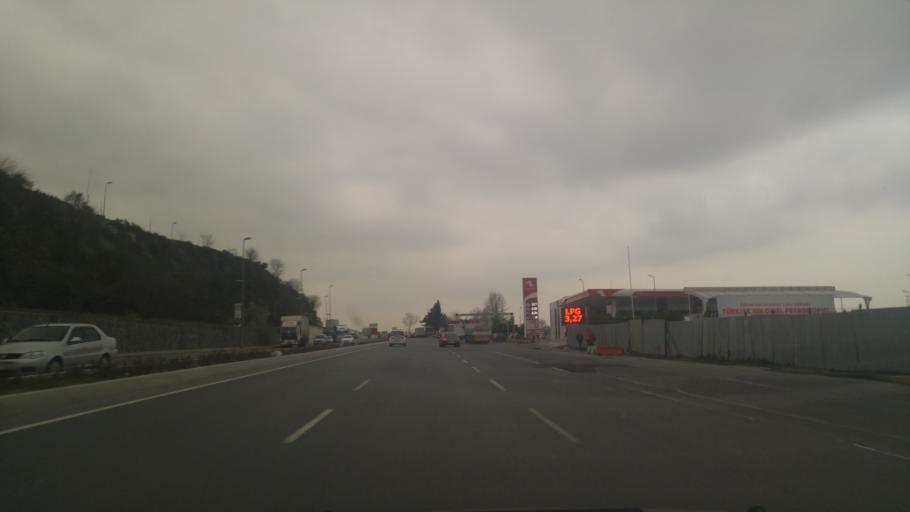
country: TR
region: Istanbul
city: Mahmutbey
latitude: 41.0153
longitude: 28.7686
